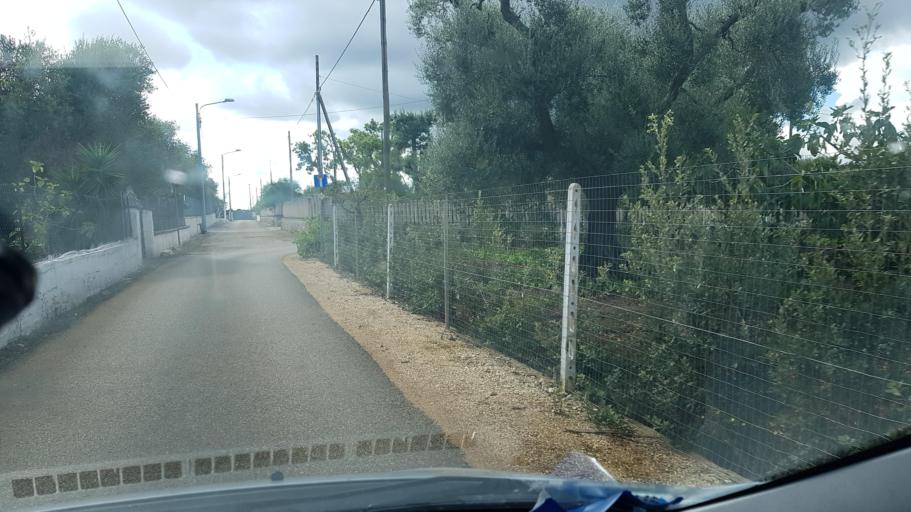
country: IT
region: Apulia
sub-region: Provincia di Brindisi
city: San Vito dei Normanni
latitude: 40.6541
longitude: 17.7343
